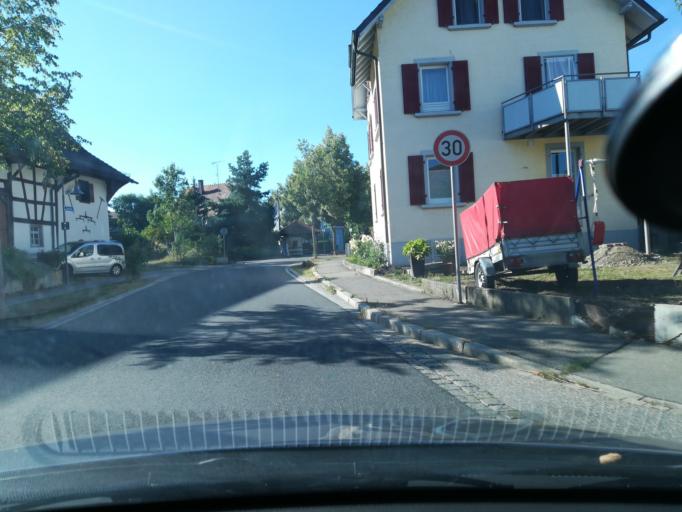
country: DE
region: Baden-Wuerttemberg
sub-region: Freiburg Region
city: Moos
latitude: 47.7367
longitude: 8.8976
